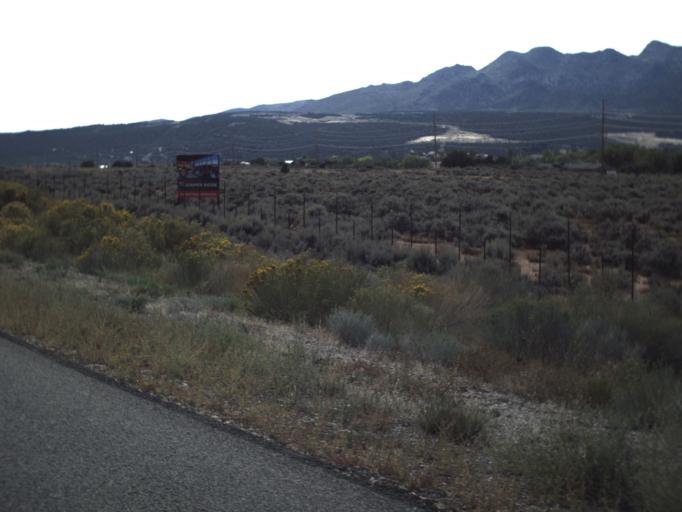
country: US
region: Utah
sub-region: Washington County
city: Toquerville
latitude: 37.4517
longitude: -113.2292
